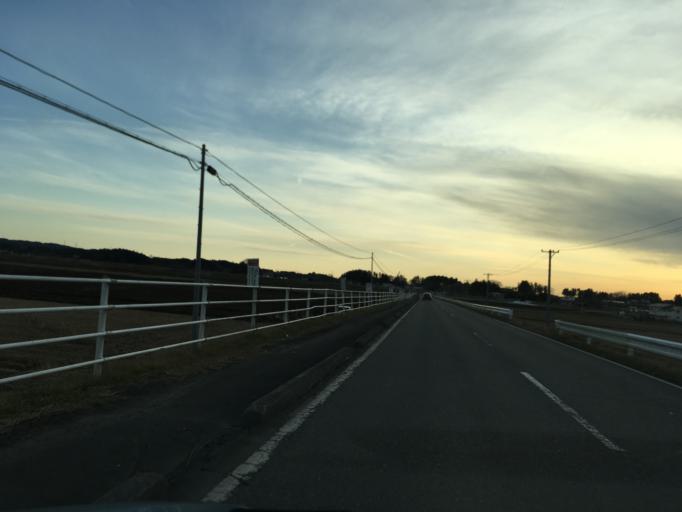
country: JP
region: Miyagi
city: Kogota
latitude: 38.6416
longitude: 141.0726
